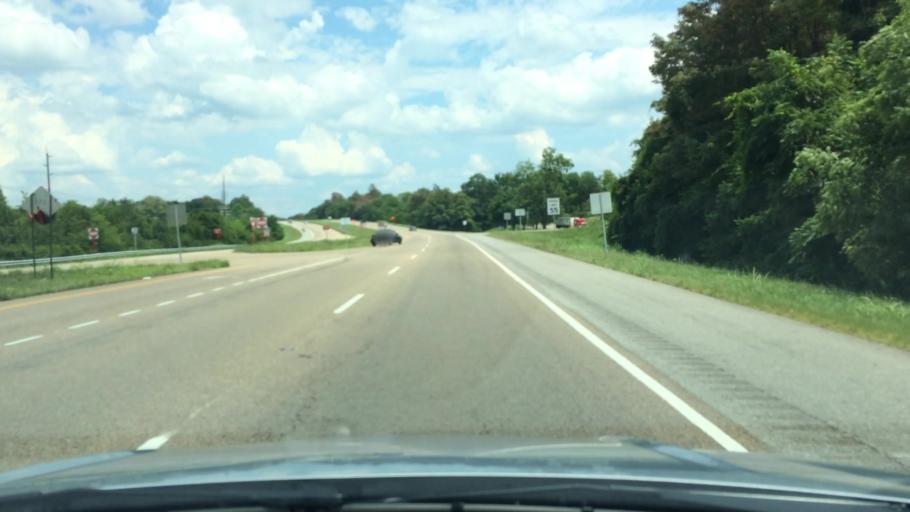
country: US
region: Tennessee
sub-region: Hamblen County
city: Morristown
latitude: 36.1796
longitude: -83.3392
